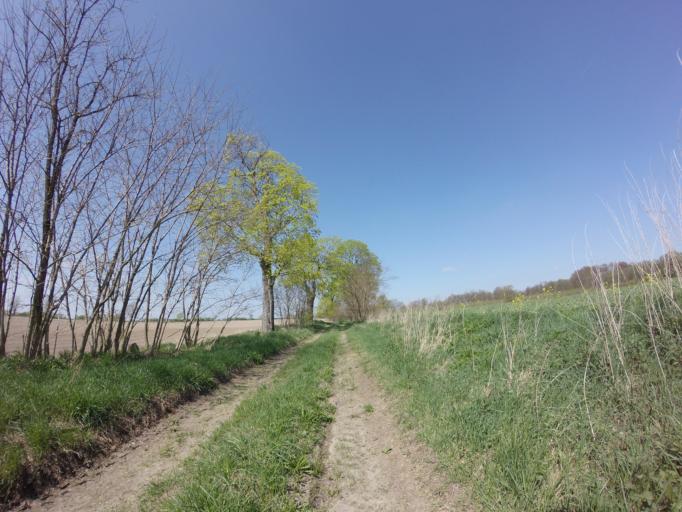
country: PL
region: West Pomeranian Voivodeship
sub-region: Powiat stargardzki
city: Suchan
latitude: 53.2205
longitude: 15.3453
